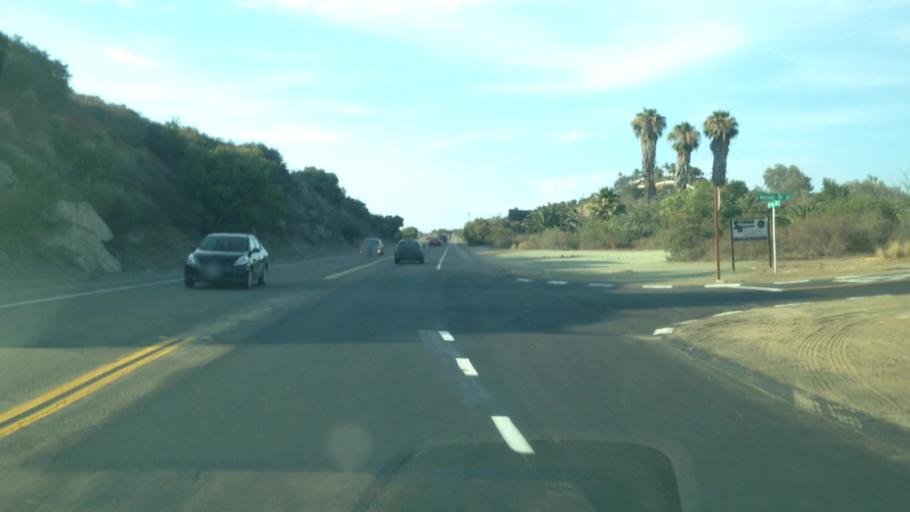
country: US
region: California
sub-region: San Diego County
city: Rainbow
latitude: 33.3916
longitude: -117.1729
